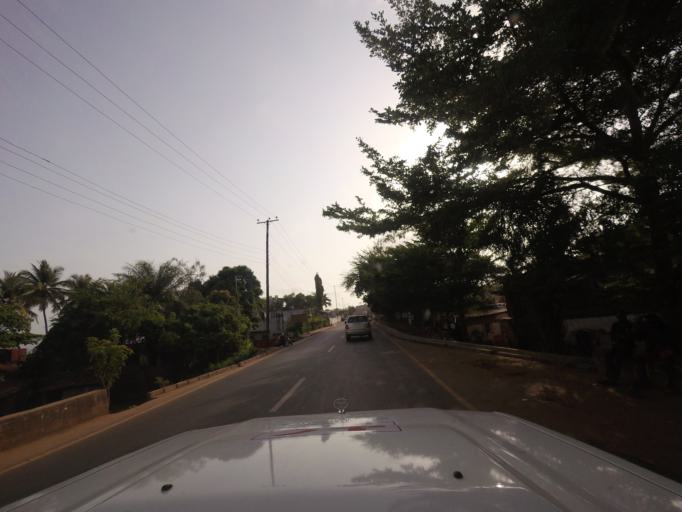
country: SL
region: Western Area
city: Freetown
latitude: 8.4929
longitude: -13.2777
